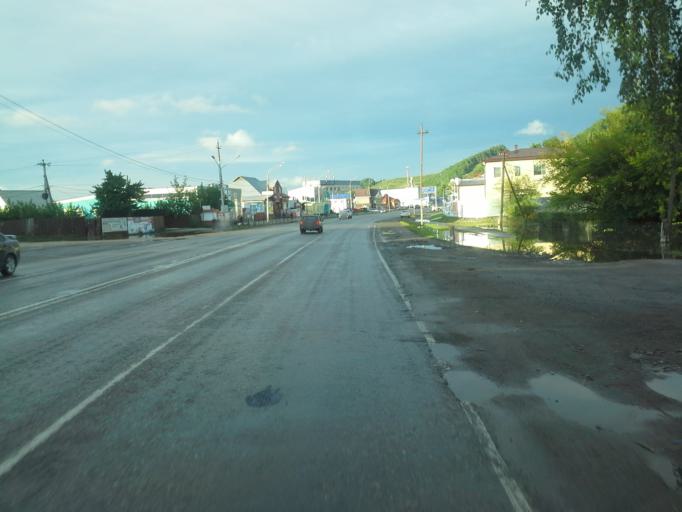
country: RU
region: Khabarovsk Krai
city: Mayma
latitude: 52.0026
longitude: 85.8976
